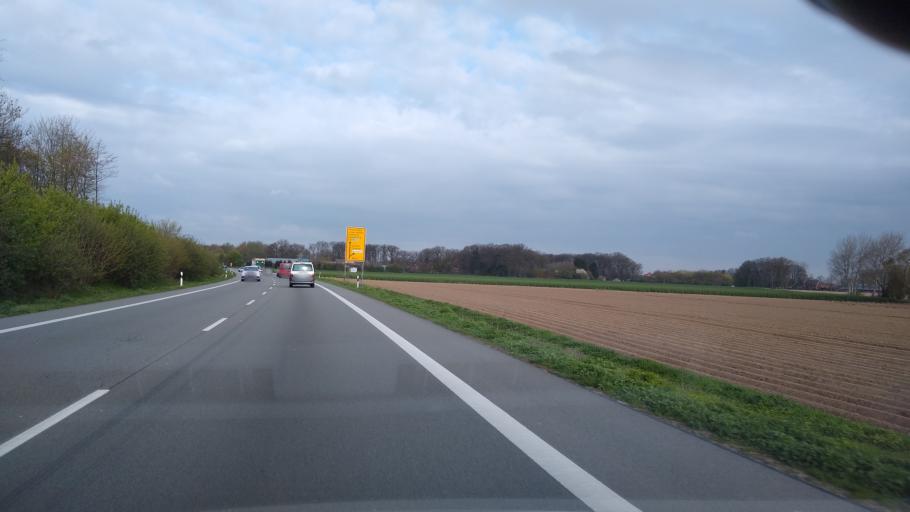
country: DE
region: Lower Saxony
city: Buehren
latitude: 52.8156
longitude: 8.2048
